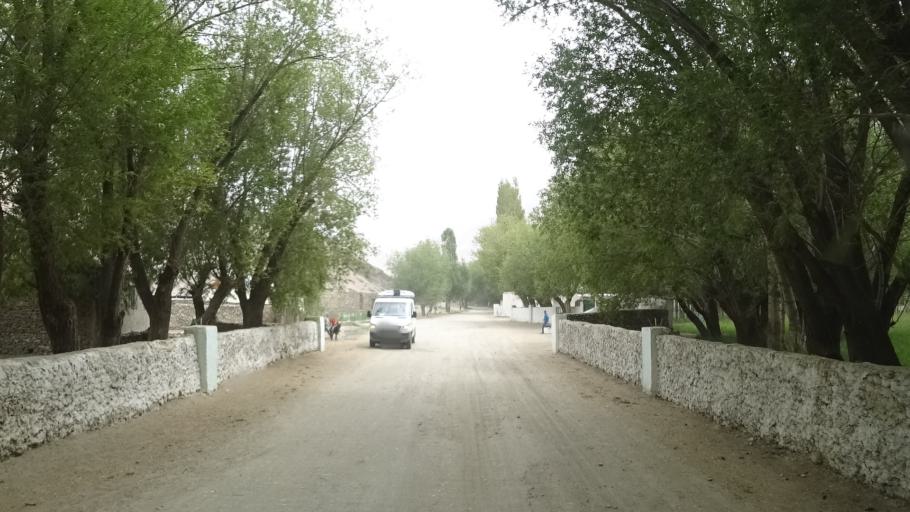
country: AF
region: Badakhshan
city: Khandud
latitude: 37.0379
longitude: 72.6494
